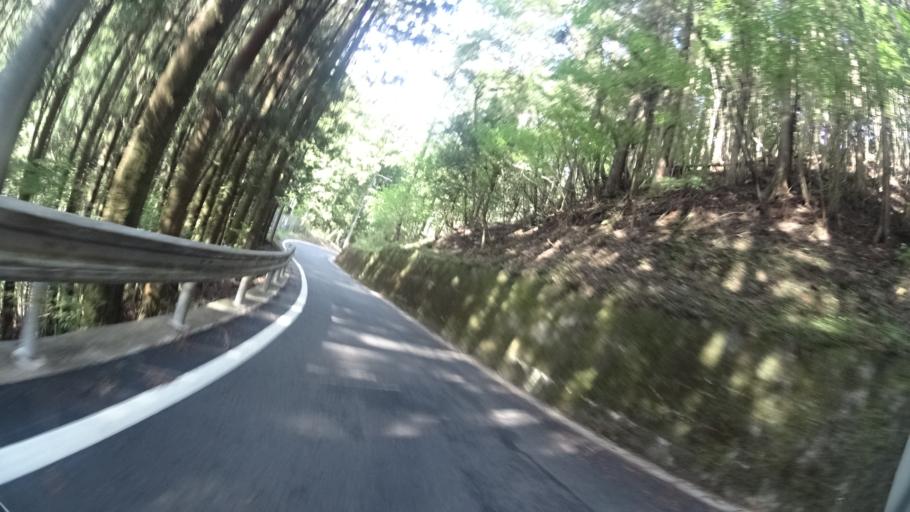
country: JP
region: Tokushima
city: Ikedacho
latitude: 33.8733
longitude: 133.9883
